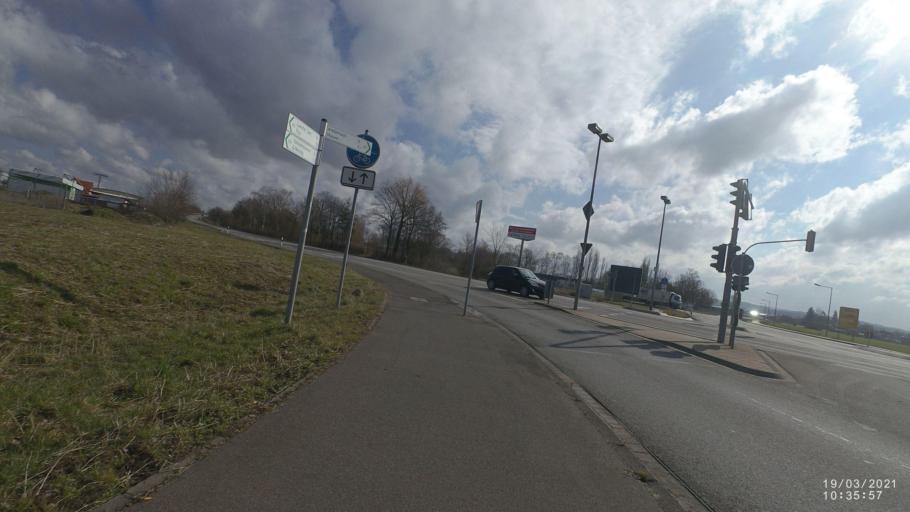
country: DE
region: Rheinland-Pfalz
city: Mendig
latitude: 50.3647
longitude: 7.2972
